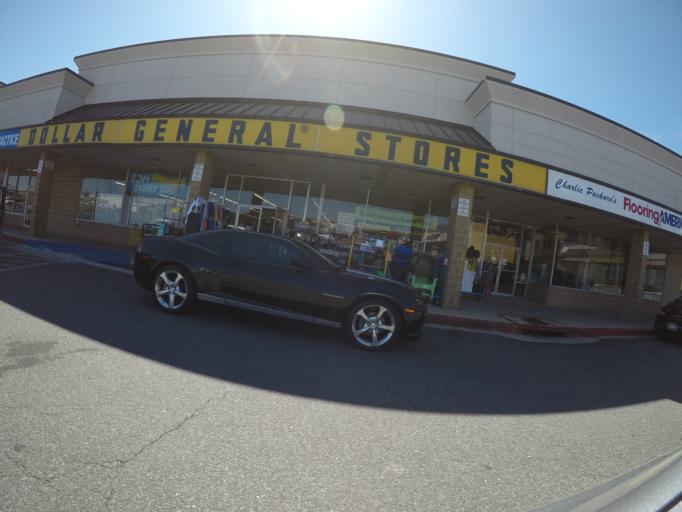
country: US
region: Maryland
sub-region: Harford County
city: Aberdeen
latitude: 39.5206
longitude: -76.1895
